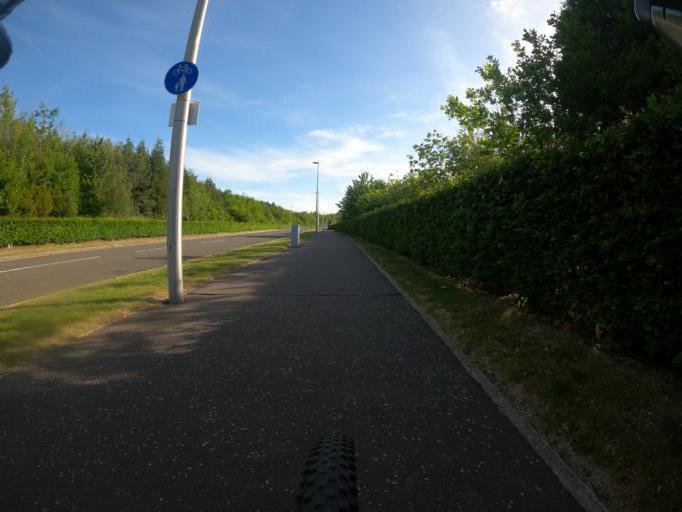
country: GB
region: Scotland
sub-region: Midlothian
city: Loanhead
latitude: 55.9199
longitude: -3.1274
